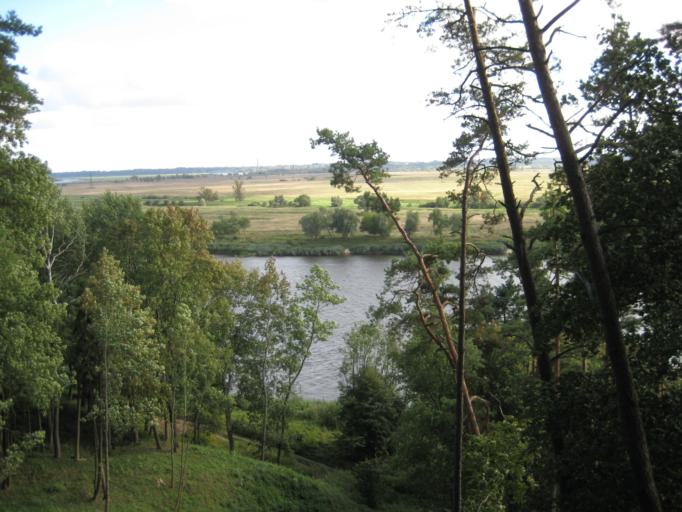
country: RU
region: Kaliningrad
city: Neman
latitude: 55.0877
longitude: 22.0228
